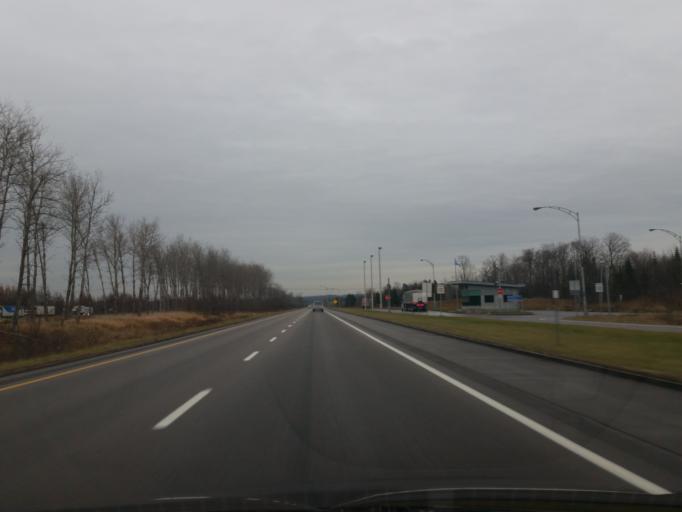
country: CA
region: Quebec
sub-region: Capitale-Nationale
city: Saint-Augustin-de-Desmaures
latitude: 46.7466
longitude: -71.5221
